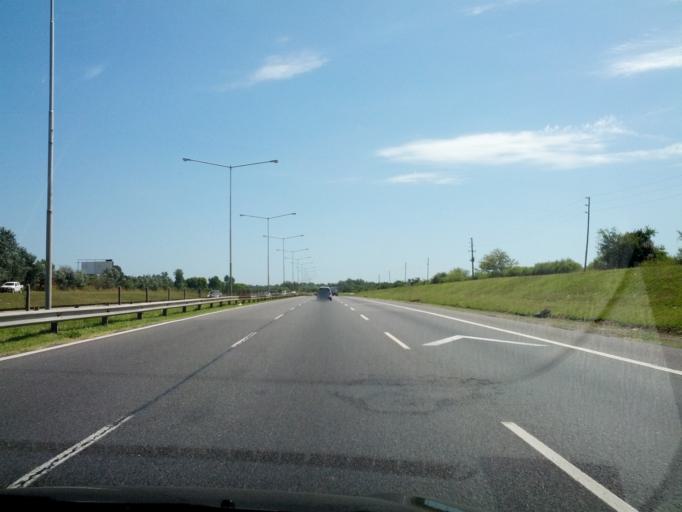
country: AR
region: Buenos Aires
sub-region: Partido de Campana
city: Campana
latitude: -34.2474
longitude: -58.9078
